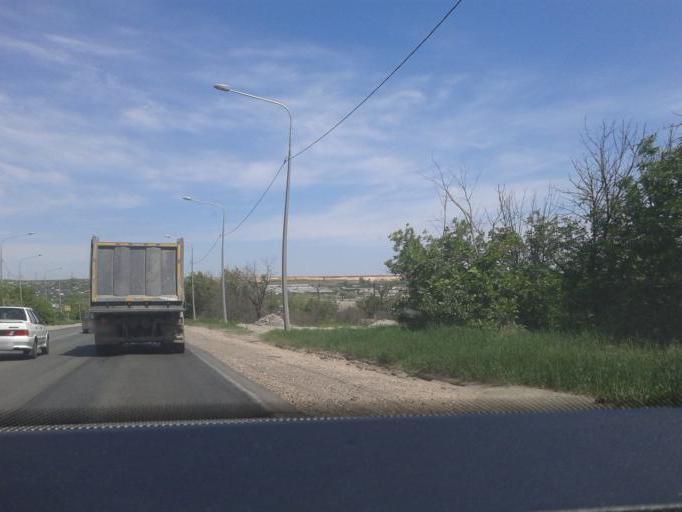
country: RU
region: Volgograd
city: Gorodishche
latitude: 48.7907
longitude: 44.5207
